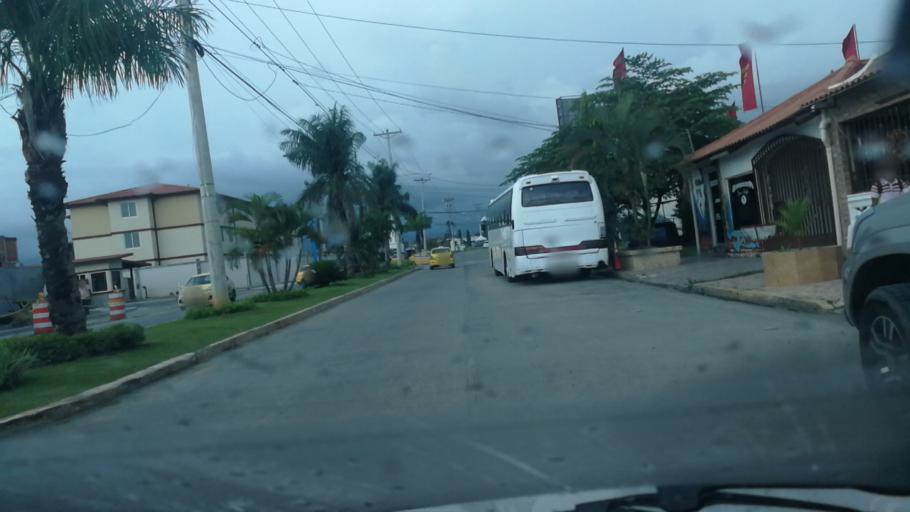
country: PA
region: Panama
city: Tocumen
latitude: 9.0732
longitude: -79.3645
